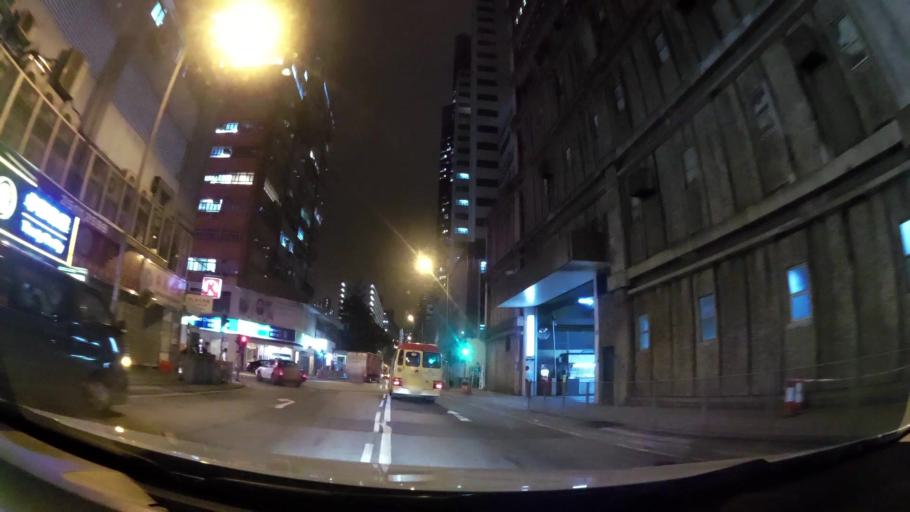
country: HK
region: Tsuen Wan
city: Tsuen Wan
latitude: 22.3631
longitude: 114.1339
